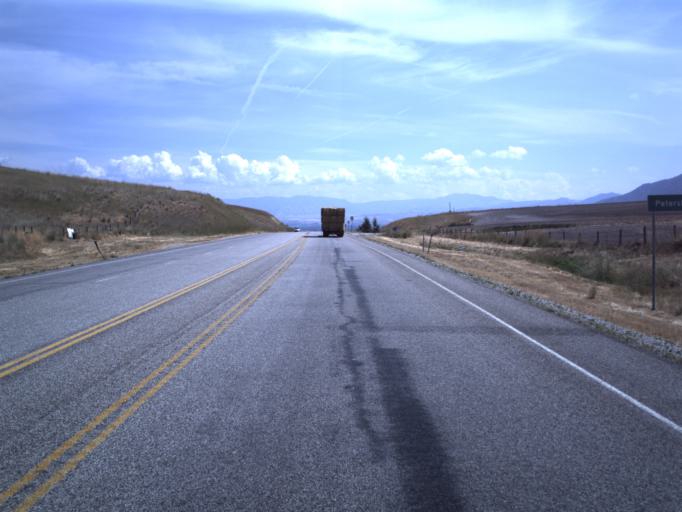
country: US
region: Utah
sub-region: Cache County
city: Mendon
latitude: 41.7719
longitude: -112.0167
